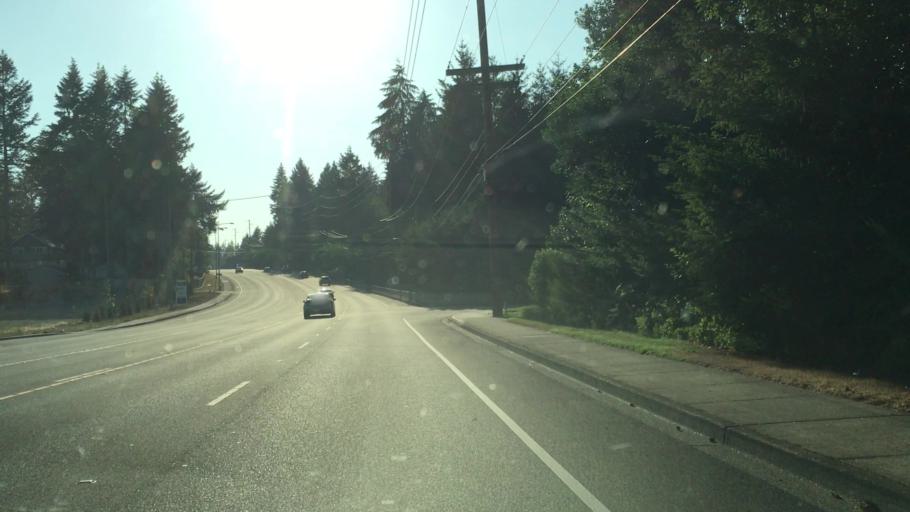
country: US
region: Washington
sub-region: Pierce County
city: Fife Heights
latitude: 47.2827
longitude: -122.3367
